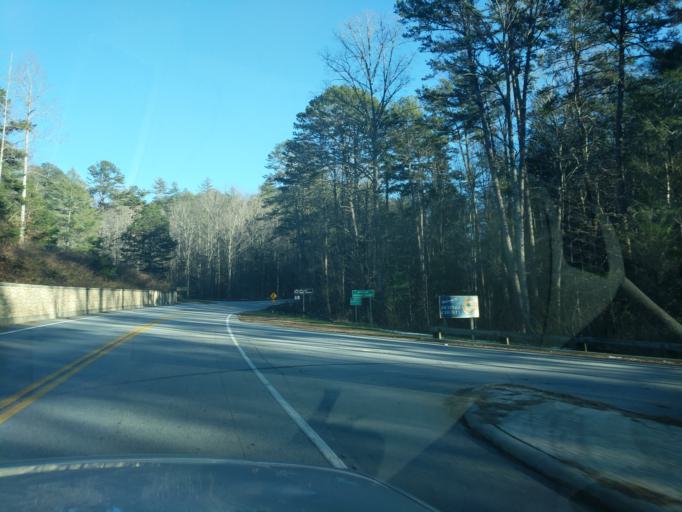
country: US
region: Georgia
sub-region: Rabun County
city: Clayton
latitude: 34.8142
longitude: -83.3064
